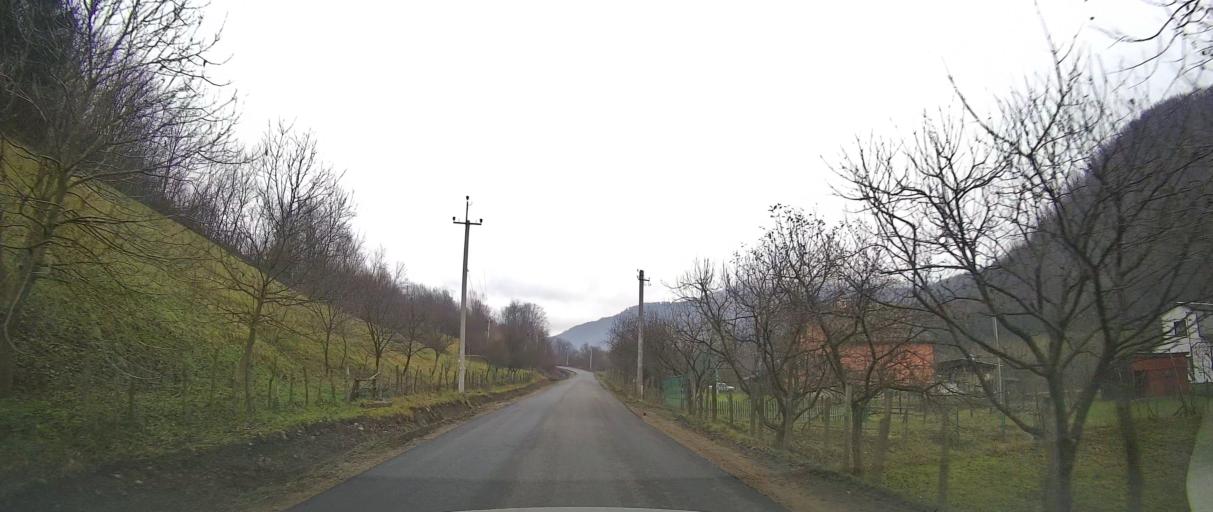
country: UA
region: Zakarpattia
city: Velykyi Bereznyi
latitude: 48.9590
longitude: 22.5477
